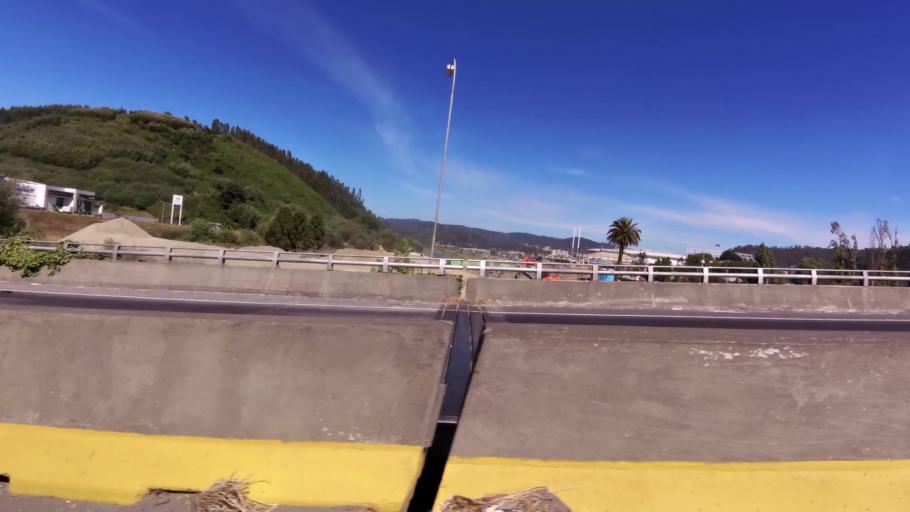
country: CL
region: Biobio
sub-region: Provincia de Concepcion
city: Concepcion
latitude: -36.8103
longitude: -73.0269
